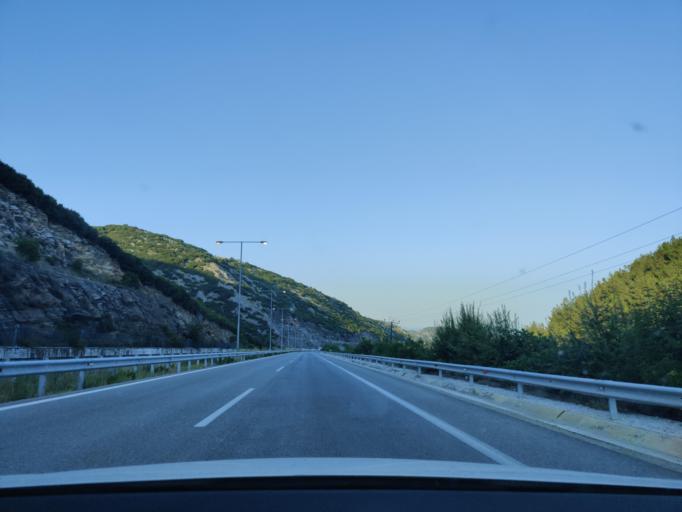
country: GR
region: East Macedonia and Thrace
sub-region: Nomos Kavalas
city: Kavala
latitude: 40.9614
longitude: 24.3951
